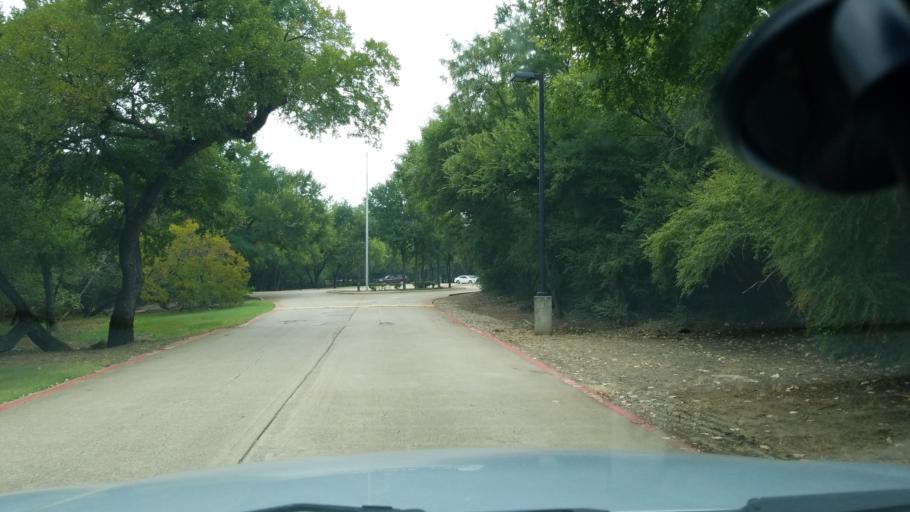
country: US
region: Texas
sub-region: Dallas County
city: Irving
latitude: 32.8546
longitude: -96.9228
